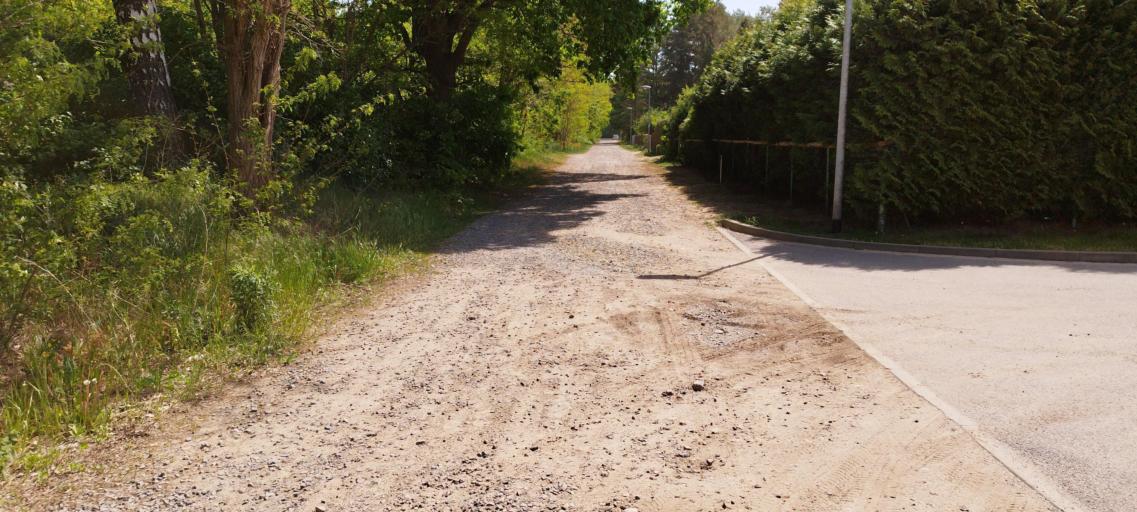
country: DE
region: Brandenburg
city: Spreenhagen
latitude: 52.3928
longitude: 13.9509
